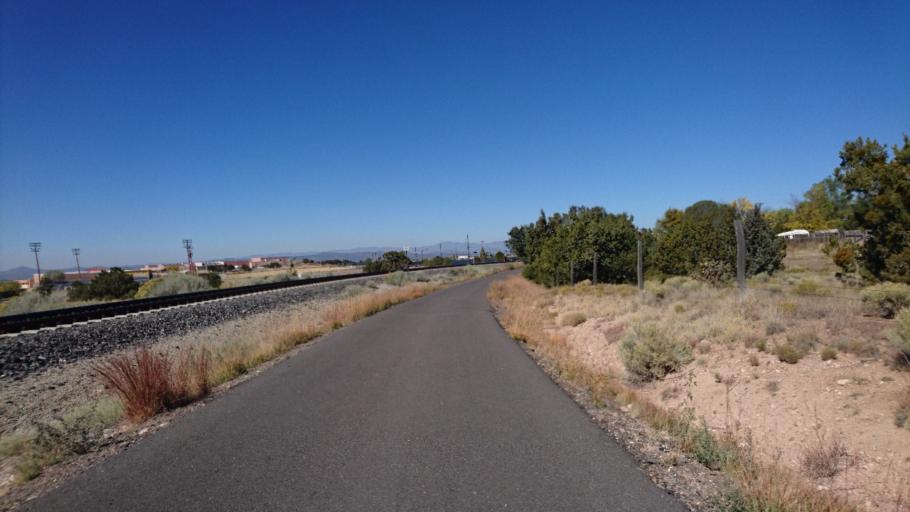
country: US
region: New Mexico
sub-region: Santa Fe County
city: Santa Fe
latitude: 35.6508
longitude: -105.9638
